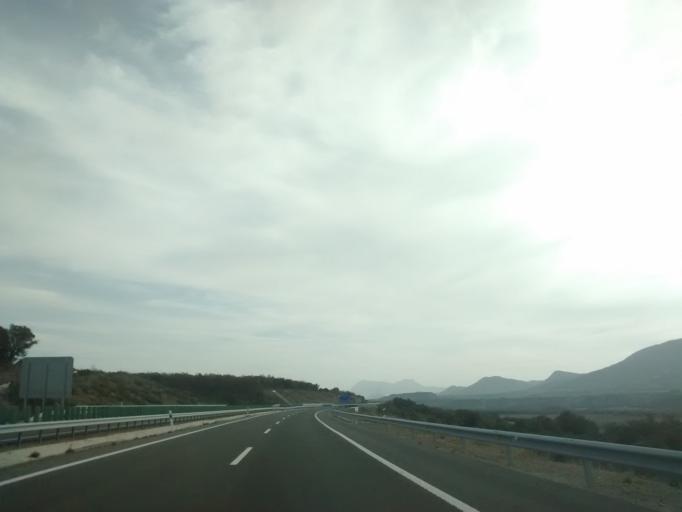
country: ES
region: Aragon
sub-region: Provincia de Zaragoza
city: Siguees
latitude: 42.6125
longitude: -0.9912
